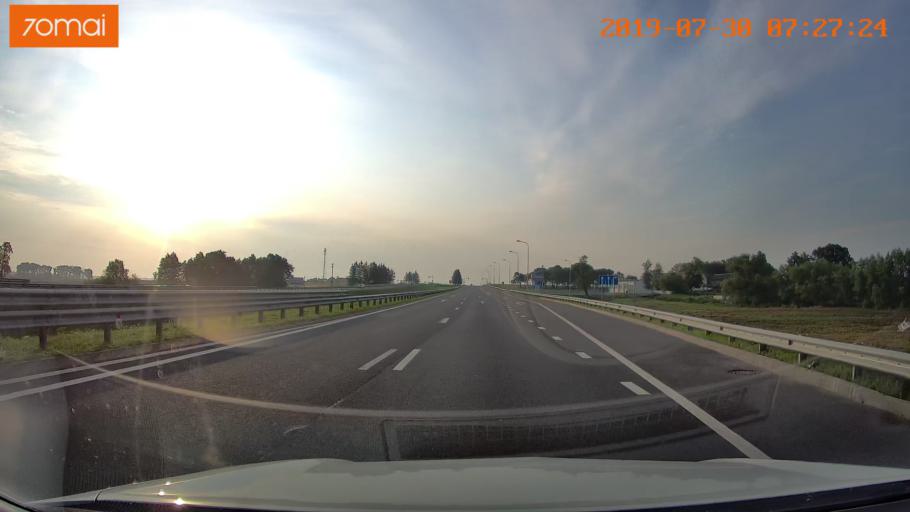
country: RU
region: Kaliningrad
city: Gvardeysk
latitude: 54.6824
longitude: 20.8865
